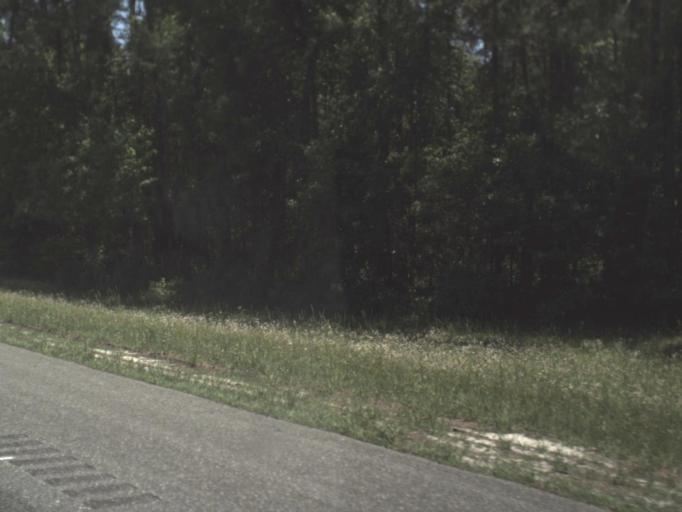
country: US
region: Florida
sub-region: Jefferson County
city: Monticello
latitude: 30.4711
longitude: -83.8180
